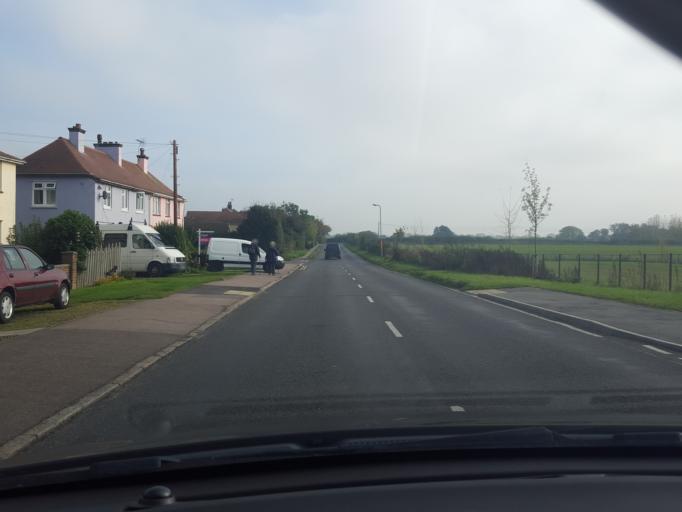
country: GB
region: England
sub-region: Essex
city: Mistley
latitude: 51.9404
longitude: 1.0916
